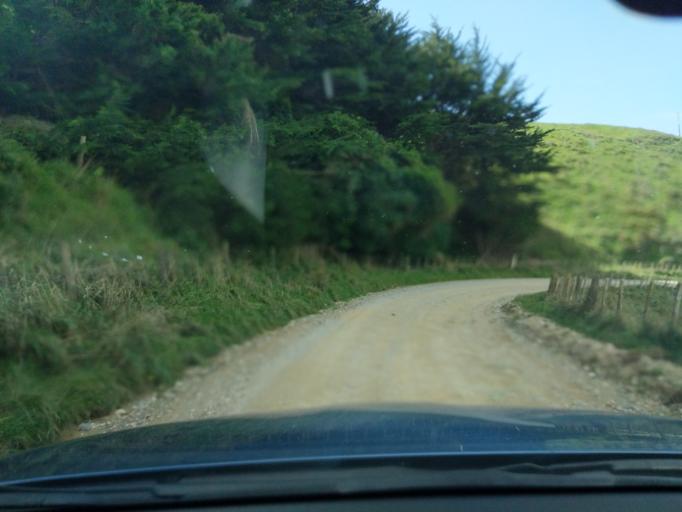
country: NZ
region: Tasman
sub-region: Tasman District
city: Takaka
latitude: -40.6466
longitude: 172.4295
